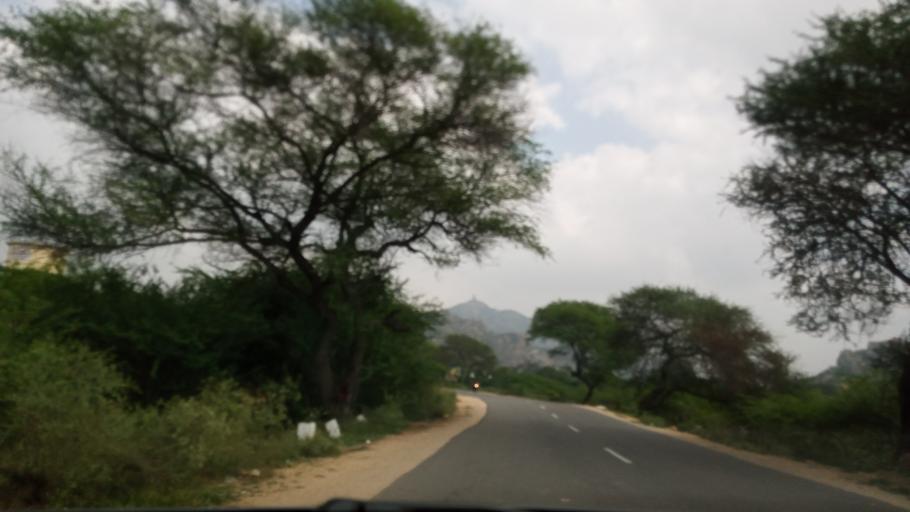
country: IN
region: Andhra Pradesh
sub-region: Chittoor
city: Madanapalle
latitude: 13.6422
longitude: 78.5606
